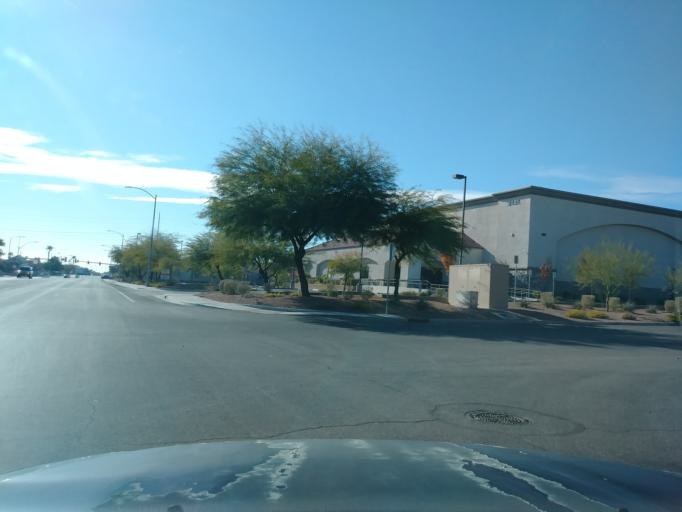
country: US
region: Nevada
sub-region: Clark County
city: Spring Valley
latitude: 36.1459
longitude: -115.2702
